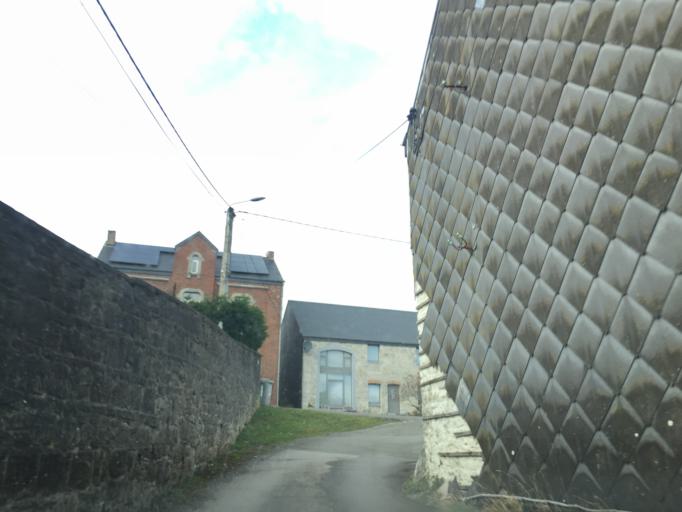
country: BE
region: Wallonia
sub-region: Province du Luxembourg
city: Durbuy
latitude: 50.3079
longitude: 5.4832
